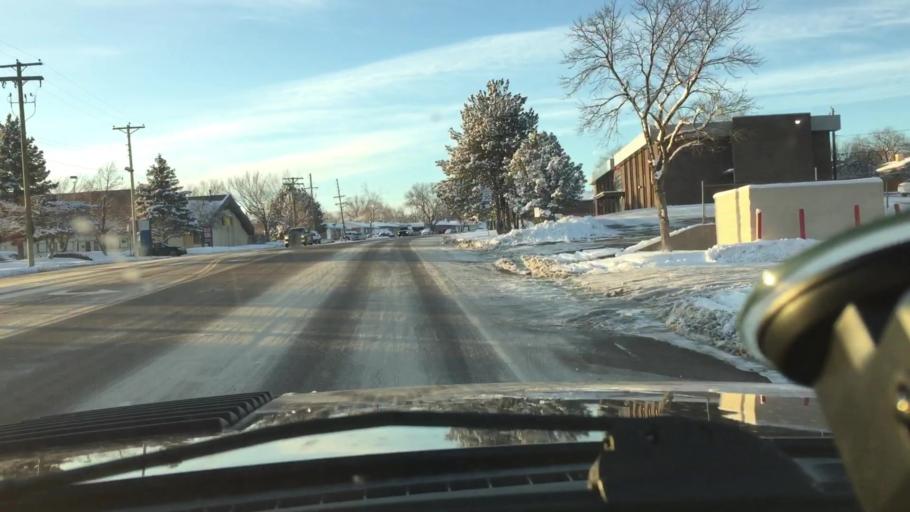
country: US
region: Colorado
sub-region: Adams County
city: Federal Heights
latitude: 39.8487
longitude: -104.9967
